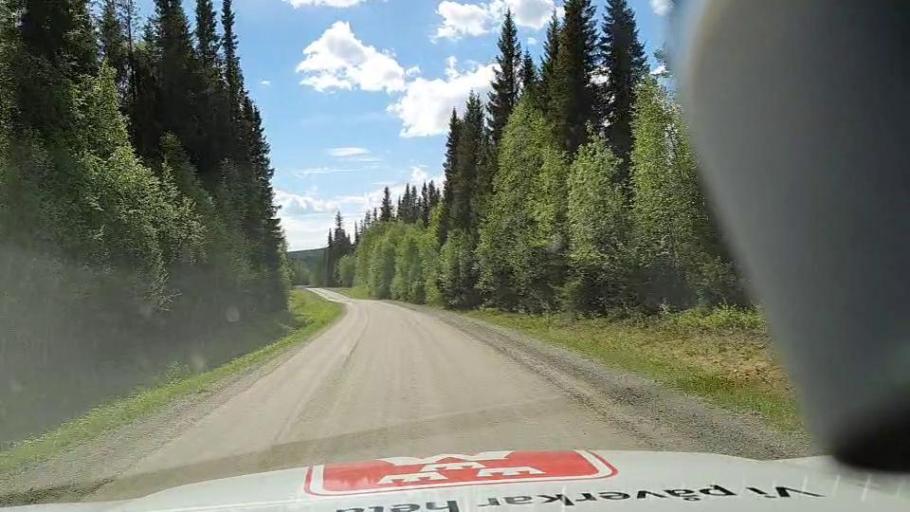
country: SE
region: Vaesterbotten
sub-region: Vilhelmina Kommun
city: Sjoberg
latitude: 64.5535
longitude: 15.8078
